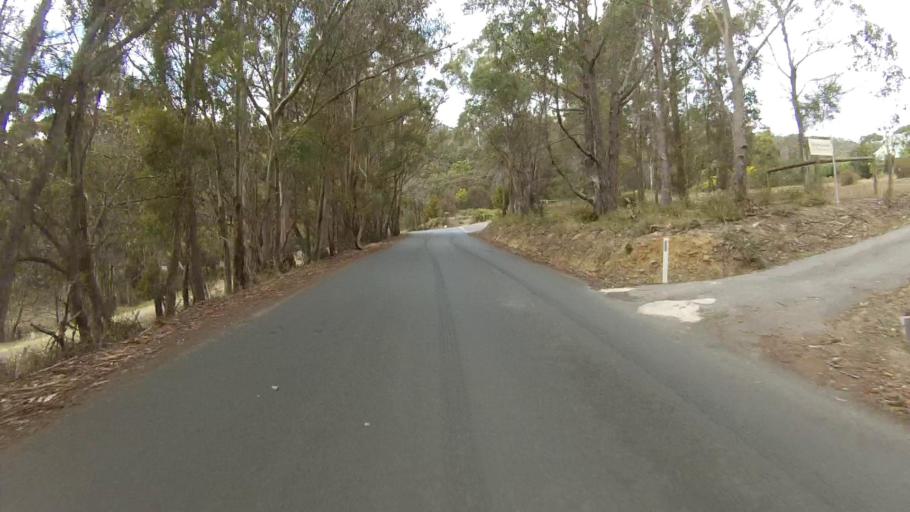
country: AU
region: Tasmania
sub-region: Kingborough
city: Blackmans Bay
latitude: -43.0228
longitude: 147.3094
